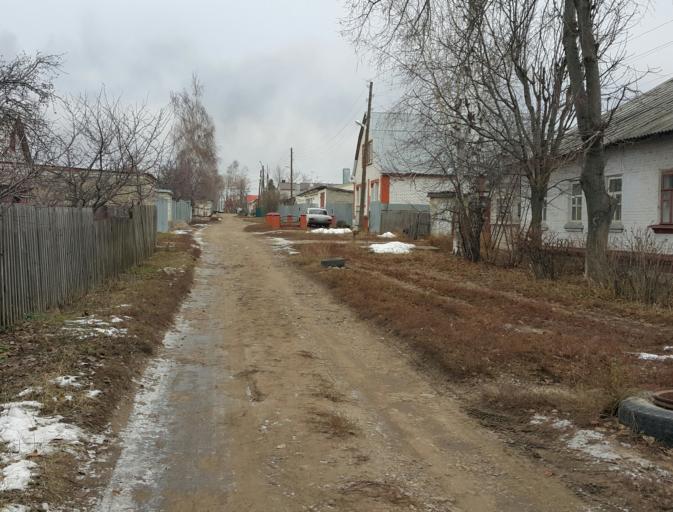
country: RU
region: Tambov
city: Pokrovo-Prigorodnoye
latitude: 52.7231
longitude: 41.4020
